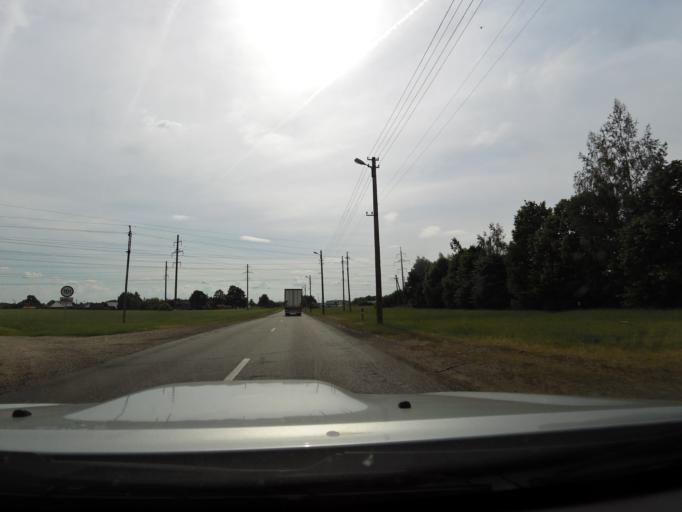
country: LT
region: Marijampoles apskritis
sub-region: Marijampole Municipality
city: Marijampole
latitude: 54.5673
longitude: 23.3887
